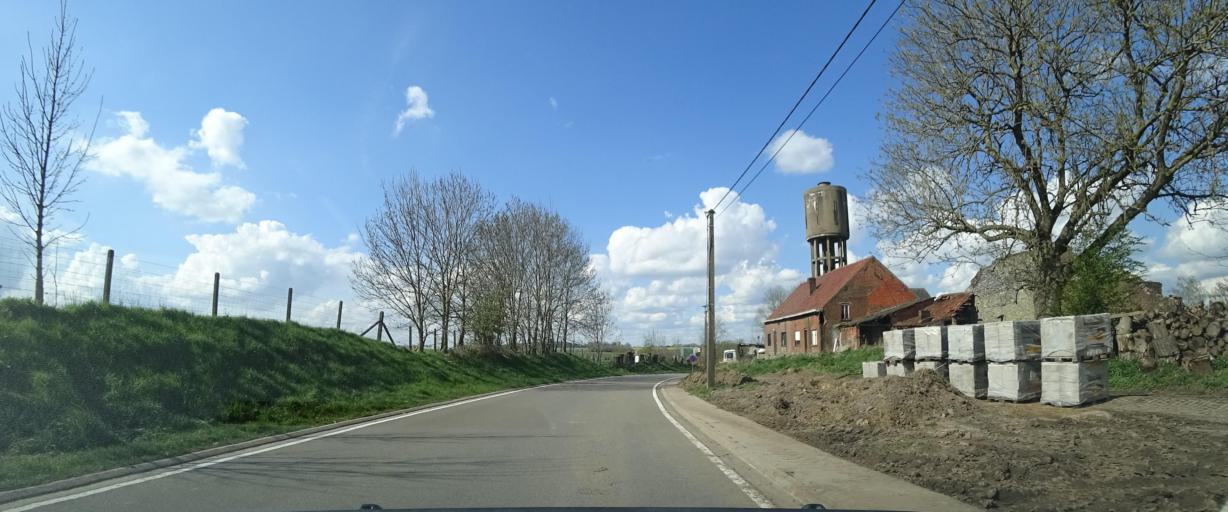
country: BE
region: Wallonia
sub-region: Province du Brabant Wallon
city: Ittre
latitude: 50.6493
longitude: 4.2199
